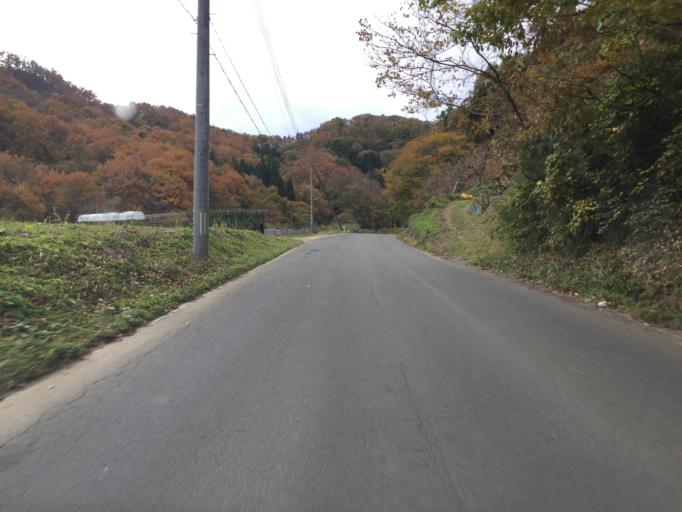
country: JP
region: Fukushima
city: Hobaramachi
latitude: 37.7465
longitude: 140.5563
